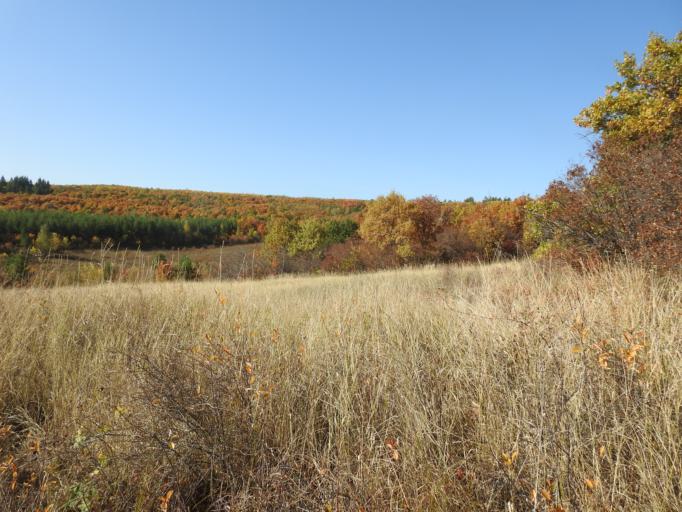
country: RU
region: Saratov
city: Baltay
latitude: 52.4838
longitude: 46.7262
